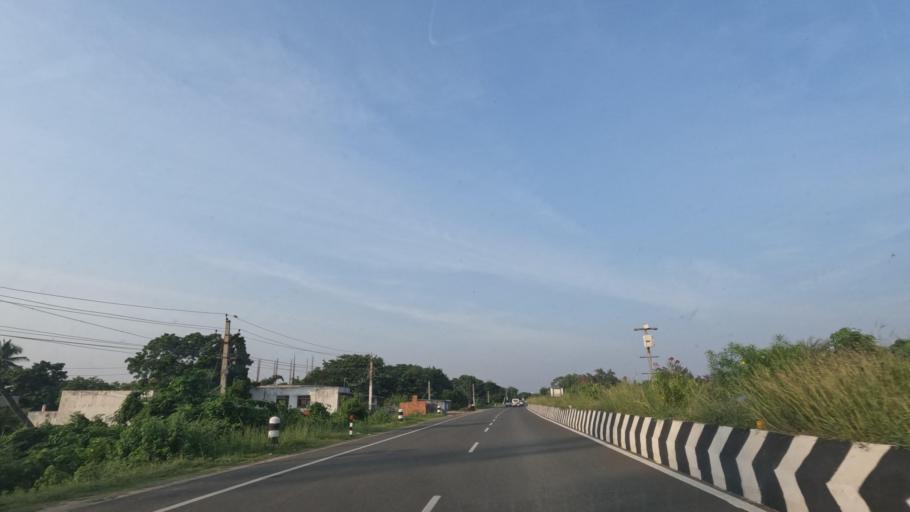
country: IN
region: Tamil Nadu
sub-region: Kancheepuram
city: Mamallapuram
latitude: 12.6430
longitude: 80.2002
